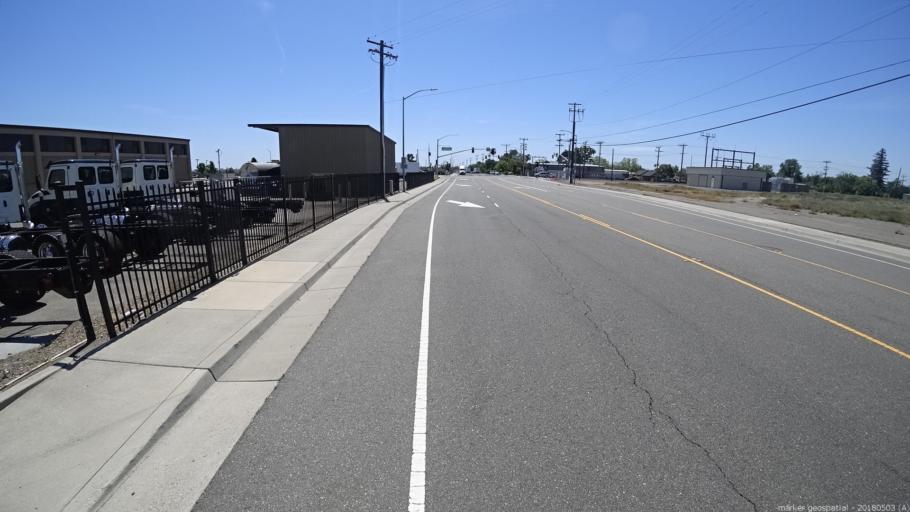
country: US
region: California
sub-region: Sacramento County
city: North Highlands
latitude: 38.6481
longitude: -121.4104
